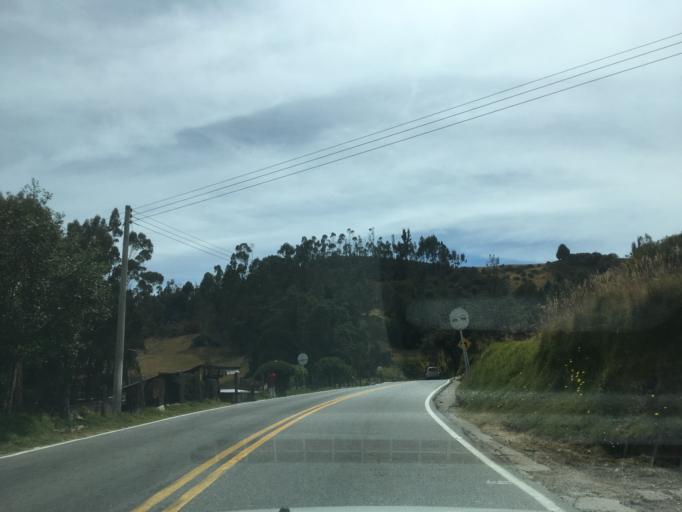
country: CO
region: Boyaca
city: Firavitoba
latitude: 5.6232
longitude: -72.9159
